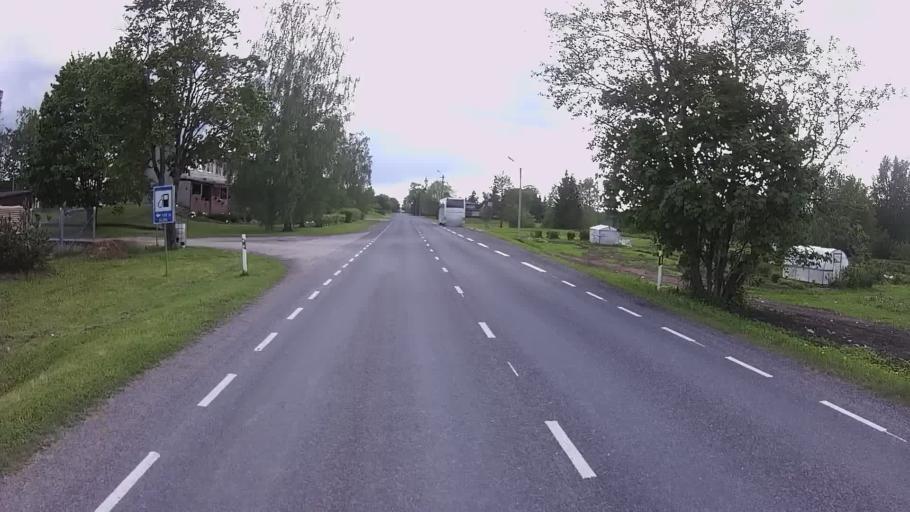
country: EE
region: Jogevamaa
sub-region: Mustvee linn
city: Mustvee
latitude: 58.9907
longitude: 26.8815
